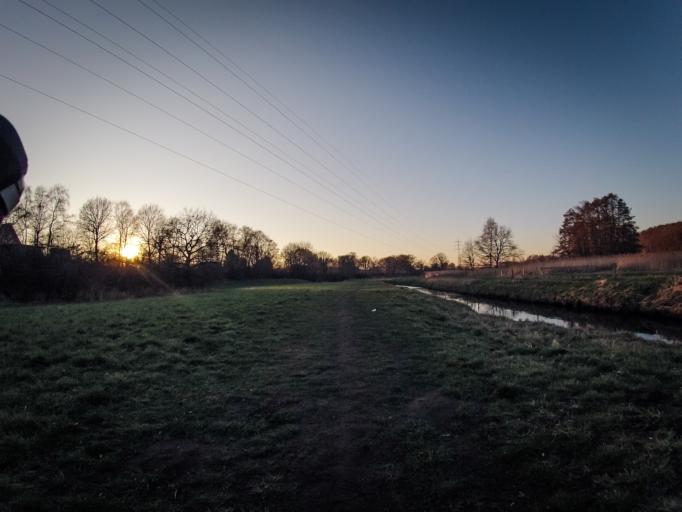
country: DE
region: Lower Saxony
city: Wallenhorst
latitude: 52.3111
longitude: 7.9800
